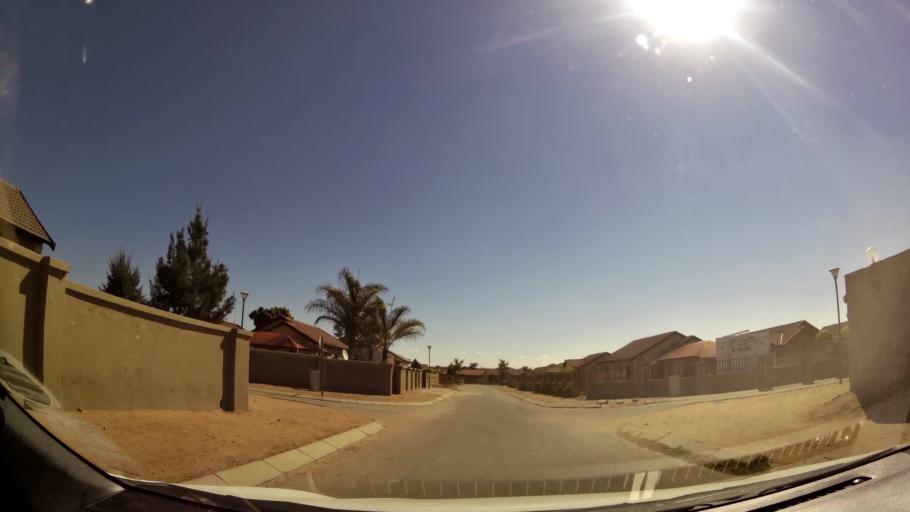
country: ZA
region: Limpopo
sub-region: Capricorn District Municipality
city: Polokwane
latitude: -23.8672
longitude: 29.4246
